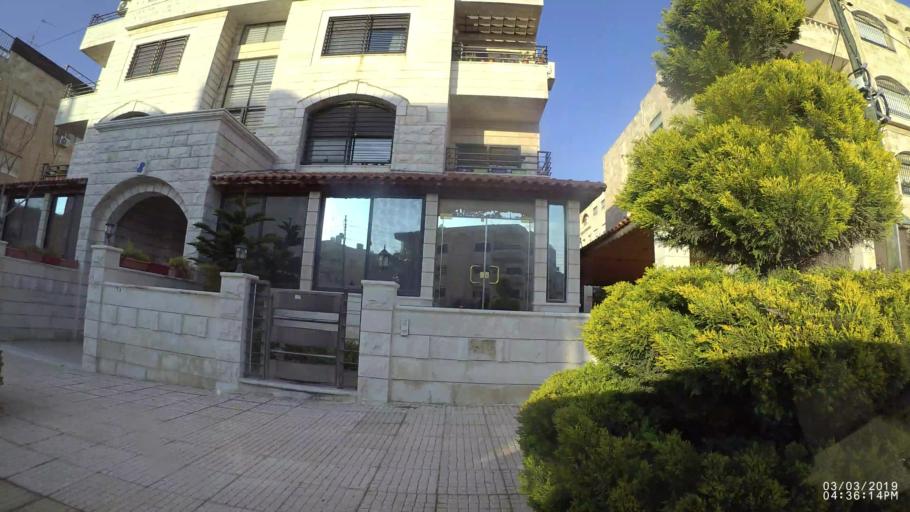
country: JO
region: Amman
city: Al Jubayhah
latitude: 31.9755
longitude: 35.8728
